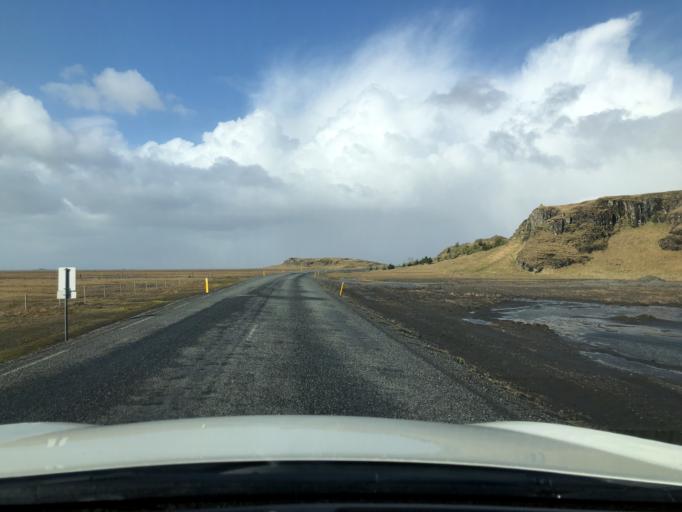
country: IS
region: East
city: Hoefn
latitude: 64.2695
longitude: -15.4990
